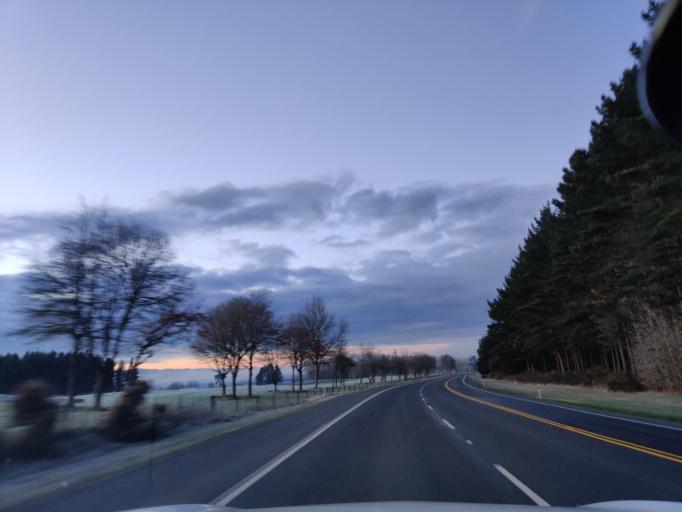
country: NZ
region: Waikato
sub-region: South Waikato District
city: Tokoroa
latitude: -38.3334
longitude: 176.0034
